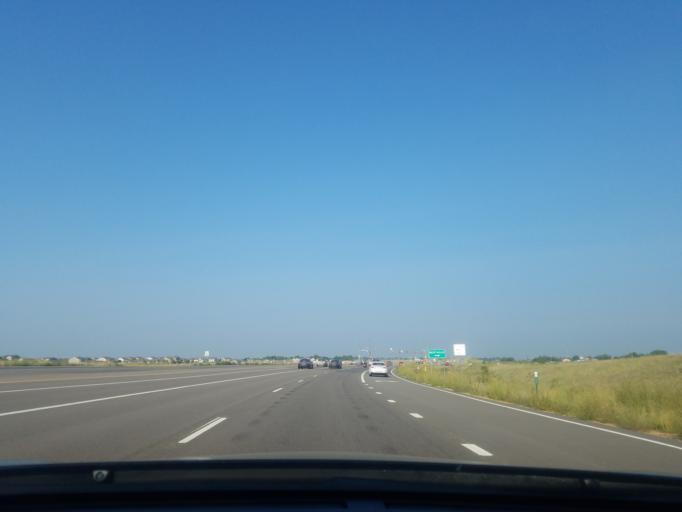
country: US
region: Colorado
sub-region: Larimer County
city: Campion
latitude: 40.3355
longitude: -105.0964
